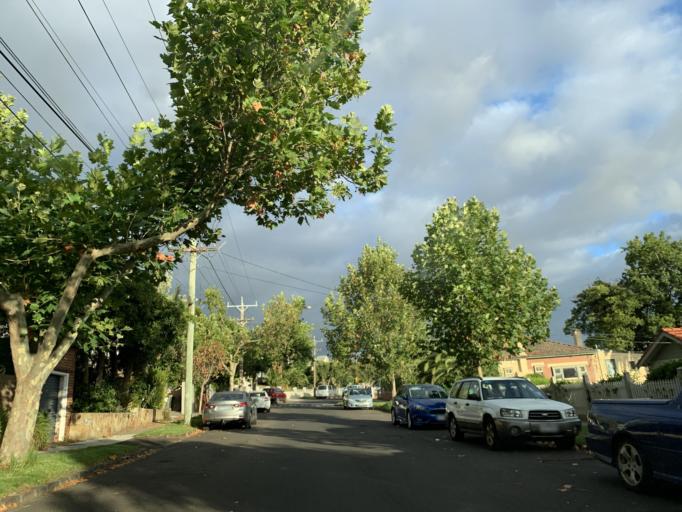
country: AU
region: Victoria
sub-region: Moonee Valley
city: Travancore
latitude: -37.7774
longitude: 144.9348
